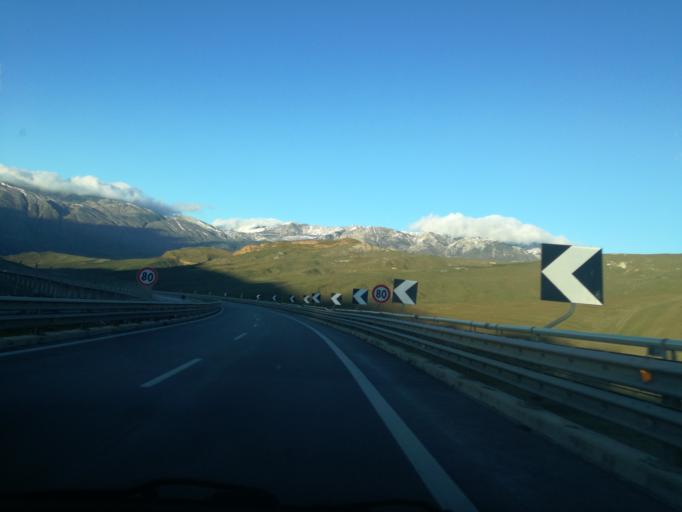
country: IT
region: Sicily
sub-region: Palermo
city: Polizzi Generosa
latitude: 37.7700
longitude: 13.9724
